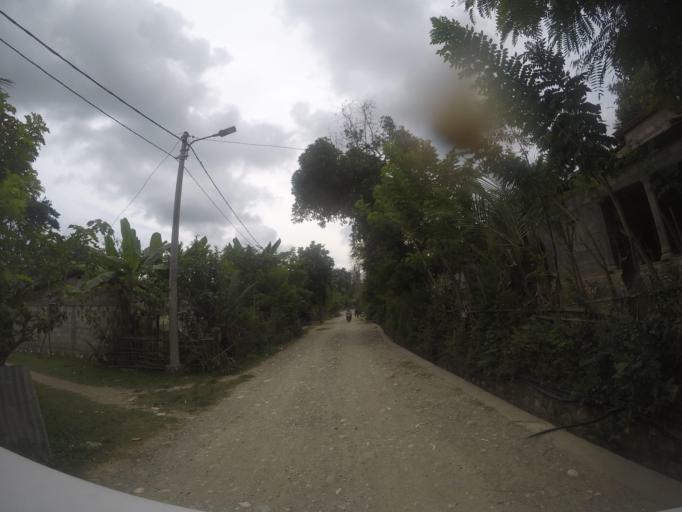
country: TL
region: Viqueque
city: Viqueque
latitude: -8.8769
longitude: 126.3644
